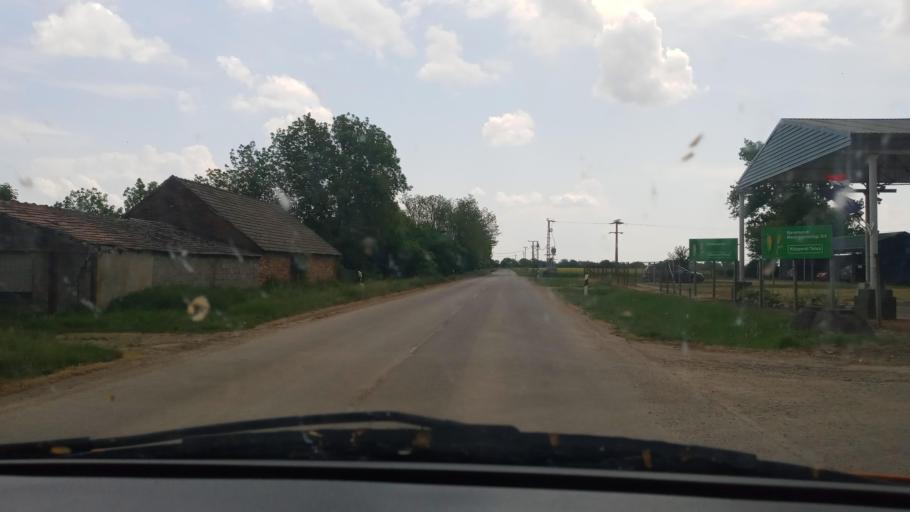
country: HU
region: Baranya
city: Beremend
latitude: 45.7726
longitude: 18.4468
